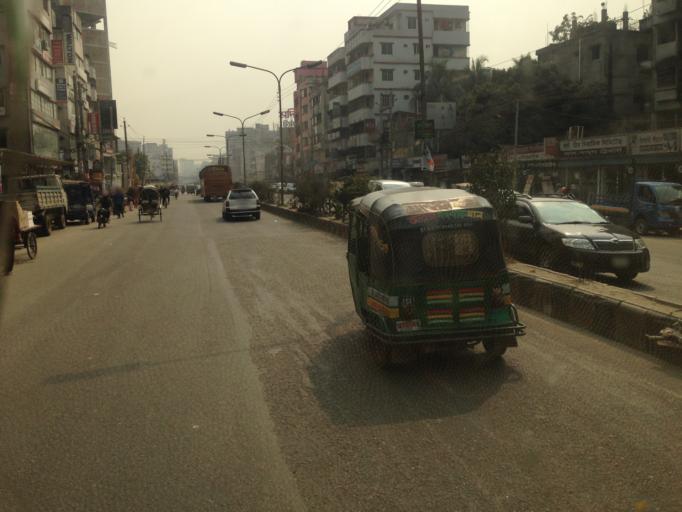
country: BD
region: Dhaka
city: Tungi
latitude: 23.8156
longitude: 90.4212
